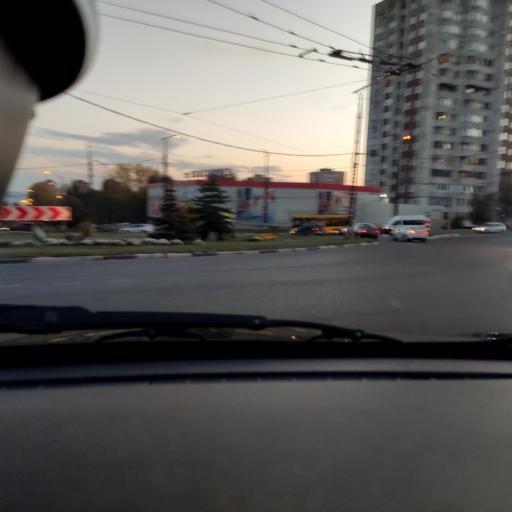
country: RU
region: Samara
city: Zhigulevsk
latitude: 53.4873
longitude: 49.4740
